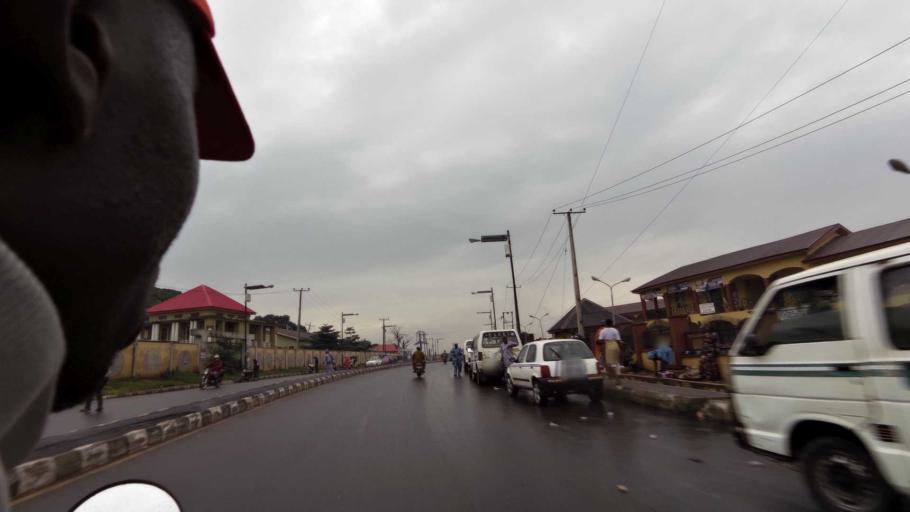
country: NG
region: Oyo
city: Ibadan
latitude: 7.3968
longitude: 3.9178
